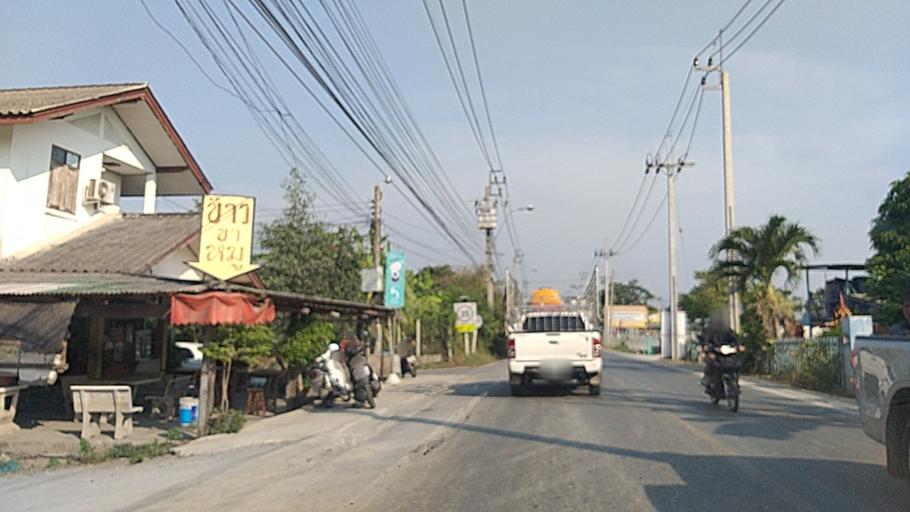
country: TH
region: Nonthaburi
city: Sai Noi
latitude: 13.9762
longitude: 100.3122
